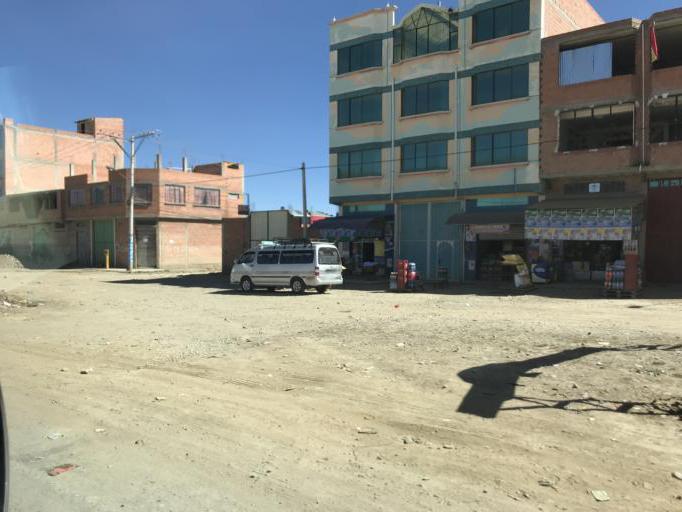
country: BO
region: La Paz
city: La Paz
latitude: -16.5068
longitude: -68.2583
